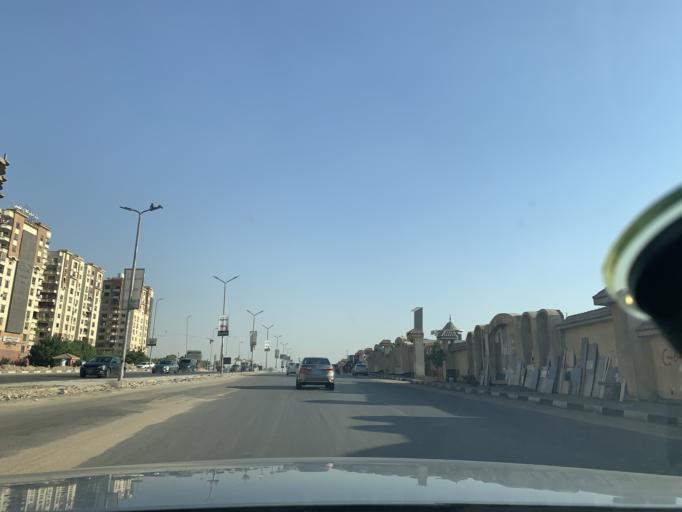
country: EG
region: Muhafazat al Qahirah
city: Cairo
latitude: 30.0333
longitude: 31.3546
